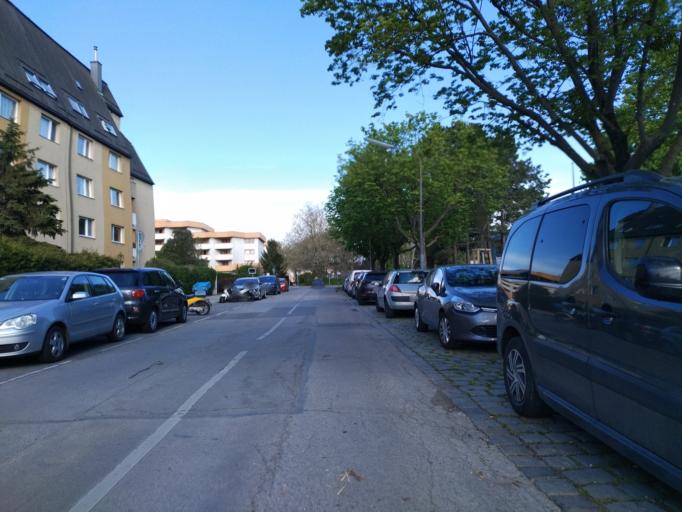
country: AT
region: Lower Austria
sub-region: Politischer Bezirk Modling
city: Vosendorf
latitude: 48.1656
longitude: 16.3034
